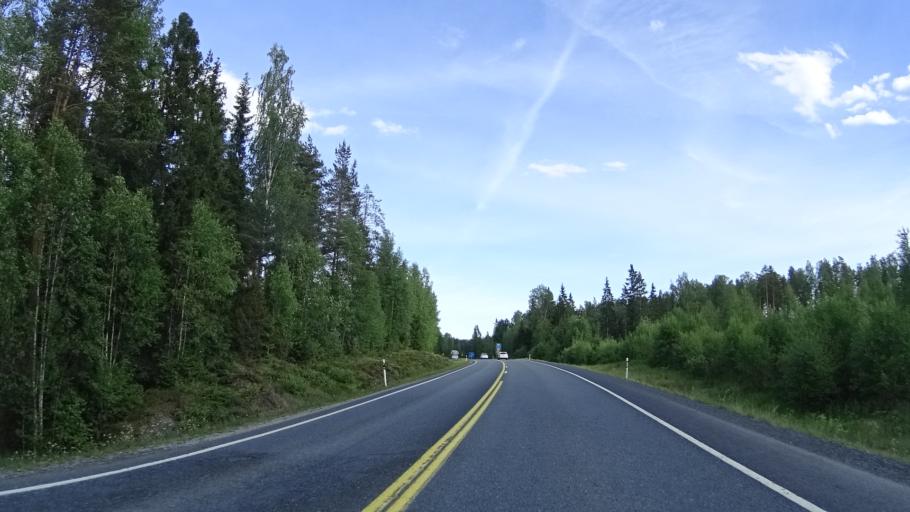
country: FI
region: Haeme
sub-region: Forssa
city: Forssa
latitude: 60.7859
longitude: 23.6559
